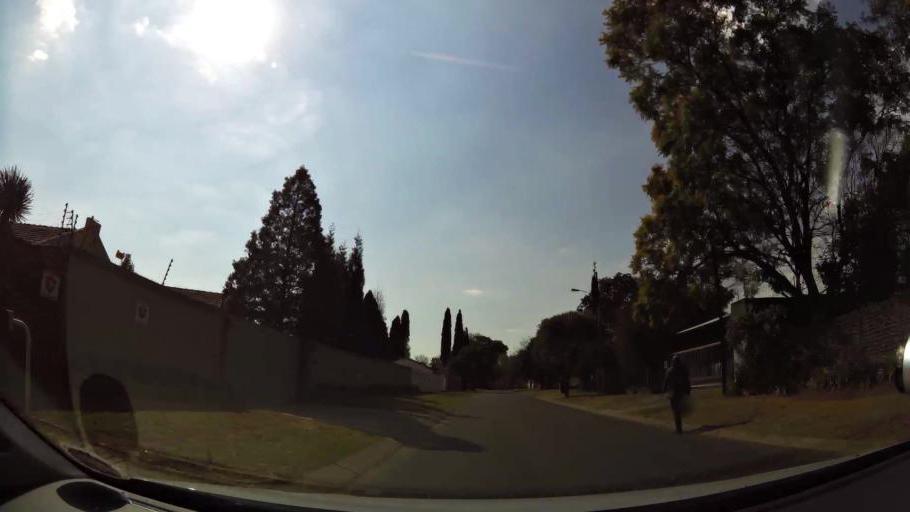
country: ZA
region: Gauteng
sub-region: City of Johannesburg Metropolitan Municipality
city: Modderfontein
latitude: -26.0802
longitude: 28.2370
